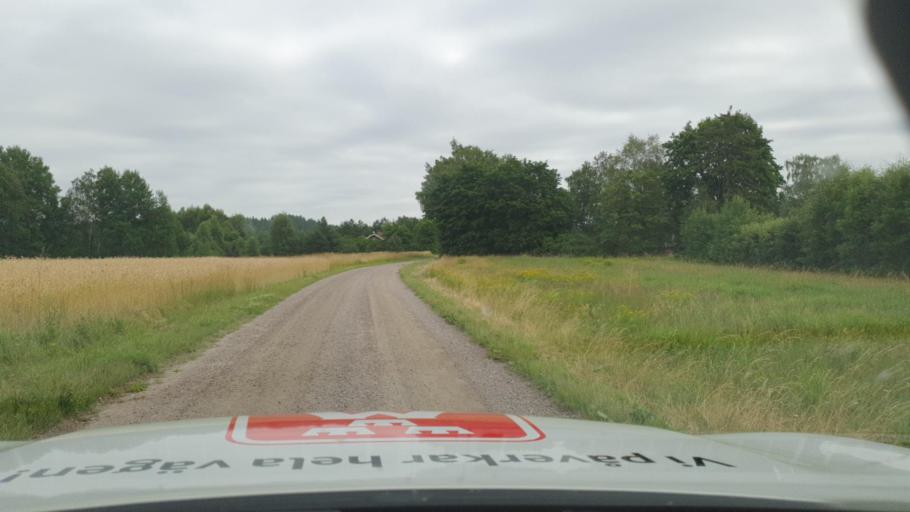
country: SE
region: Vaestra Goetaland
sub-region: Skovde Kommun
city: Skultorp
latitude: 58.2333
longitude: 13.8417
